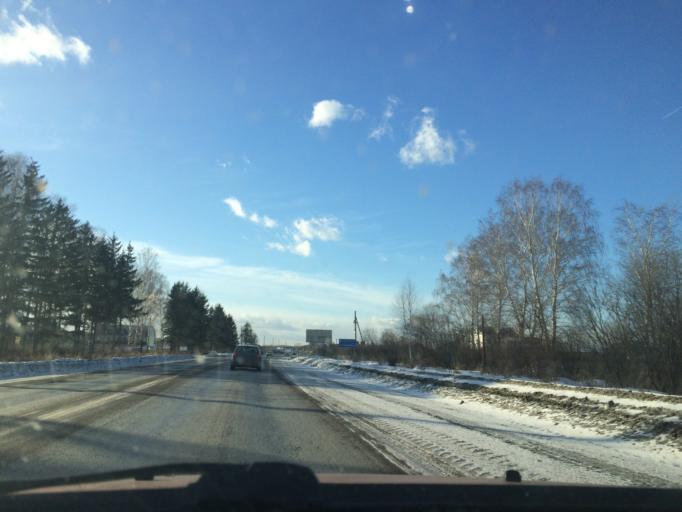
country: RU
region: Sverdlovsk
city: Istok
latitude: 56.7732
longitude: 60.8482
